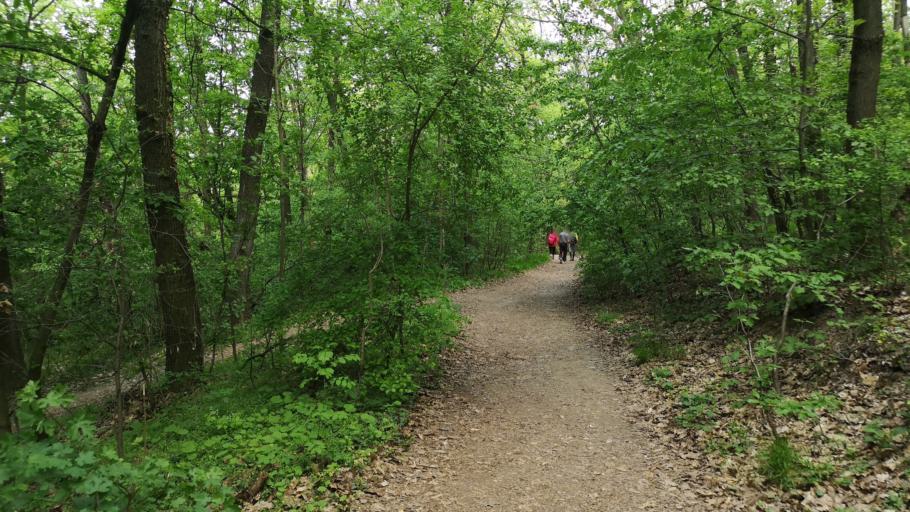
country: SK
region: Nitriansky
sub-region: Okres Nitra
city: Nitra
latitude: 48.3418
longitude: 18.0907
